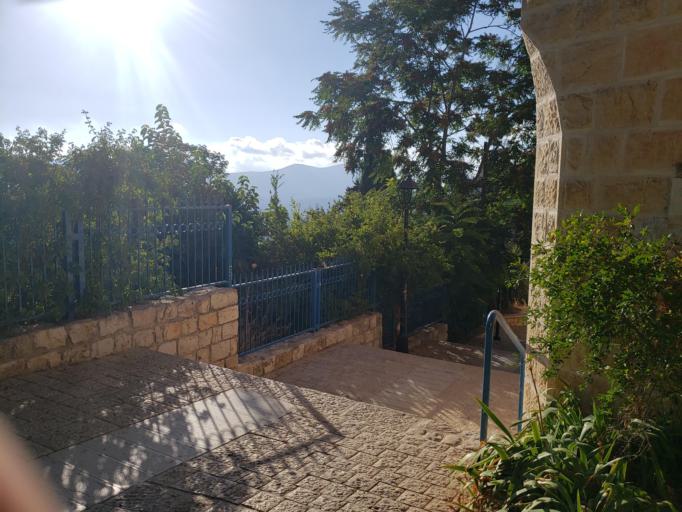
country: IL
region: Northern District
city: Safed
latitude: 32.9650
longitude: 35.4938
